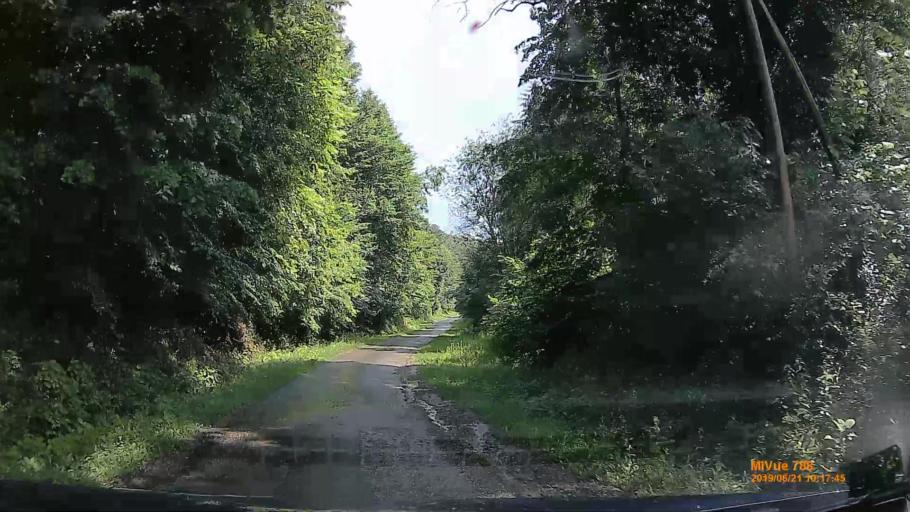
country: HU
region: Baranya
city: Buekkoesd
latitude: 46.1977
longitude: 17.9605
